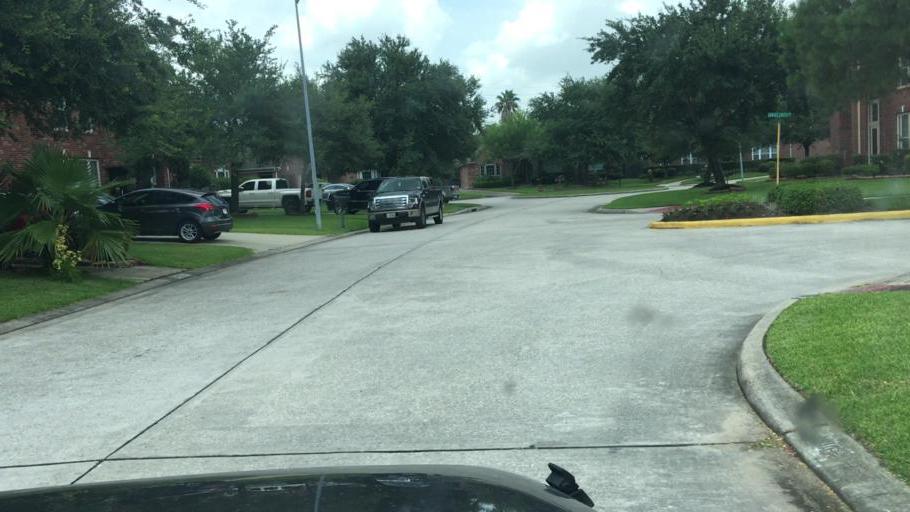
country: US
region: Texas
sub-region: Harris County
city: Atascocita
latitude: 29.9829
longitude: -95.1698
